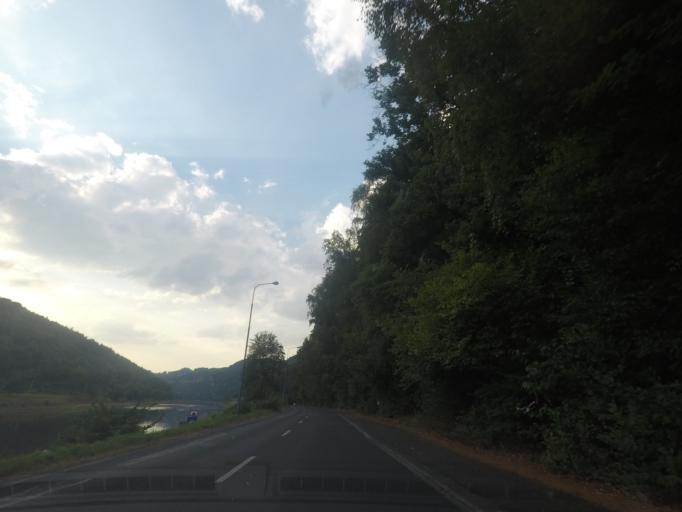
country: DE
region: Saxony
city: Bad Schandau
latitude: 50.8846
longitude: 14.2369
